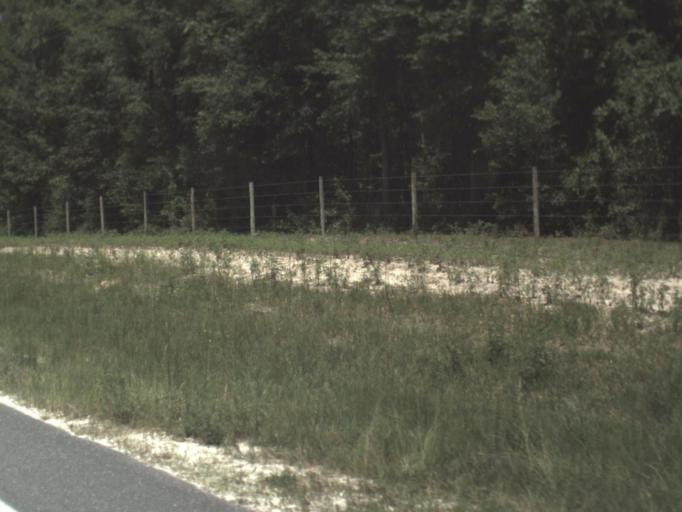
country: US
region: Florida
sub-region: Gilchrist County
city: Trenton
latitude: 29.8440
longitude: -82.8653
